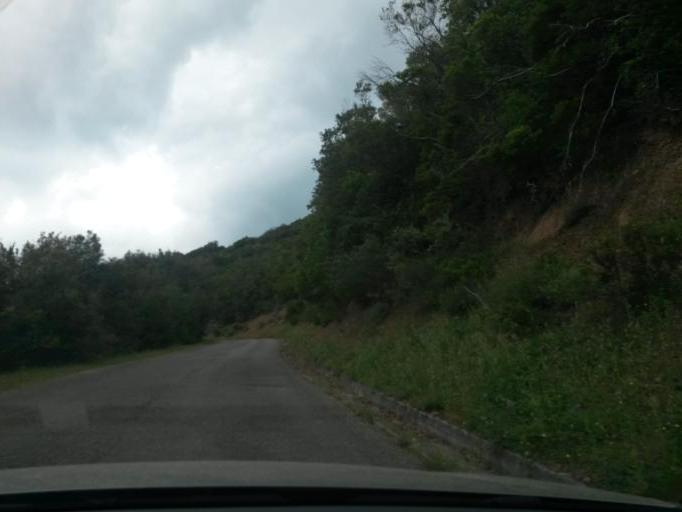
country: IT
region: Tuscany
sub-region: Provincia di Livorno
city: Rio nell'Elba
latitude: 42.8232
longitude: 10.3939
